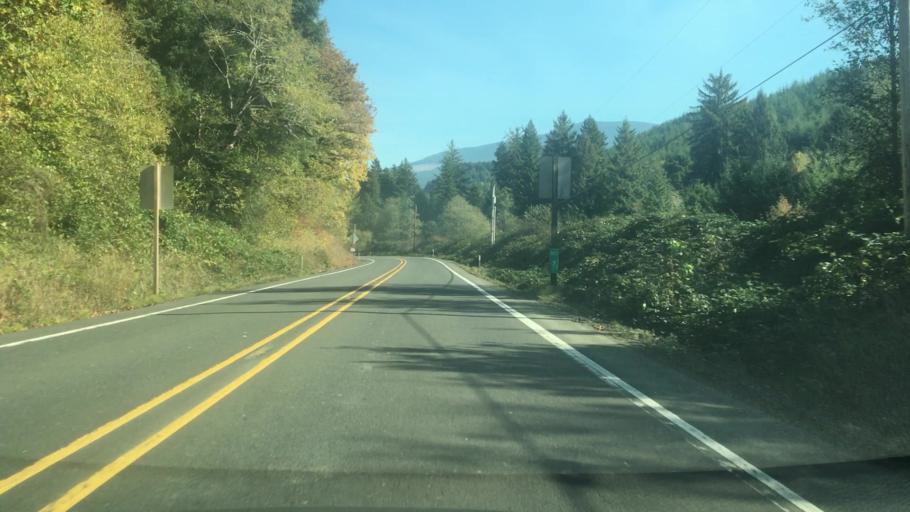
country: US
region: Oregon
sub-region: Lincoln County
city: Rose Lodge
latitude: 45.0211
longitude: -123.8516
